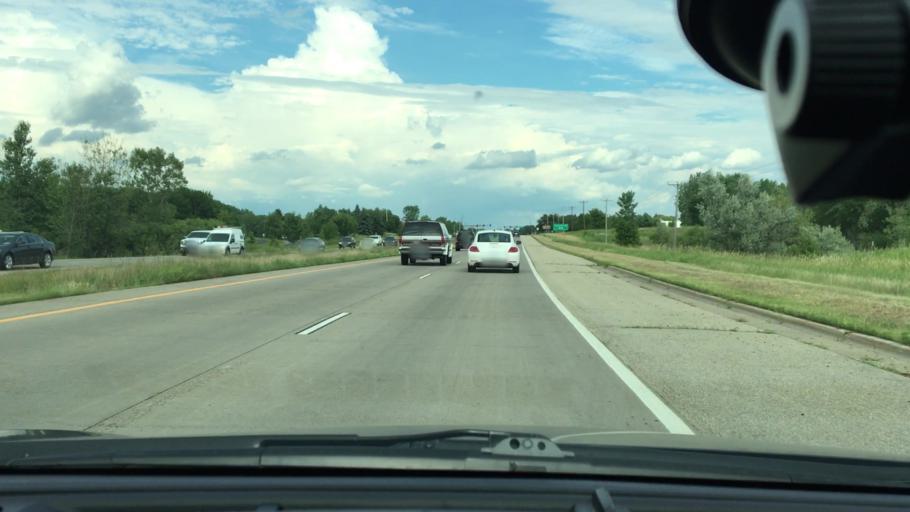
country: US
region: Minnesota
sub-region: Carver County
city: Chanhassen
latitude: 44.8630
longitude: -93.5682
